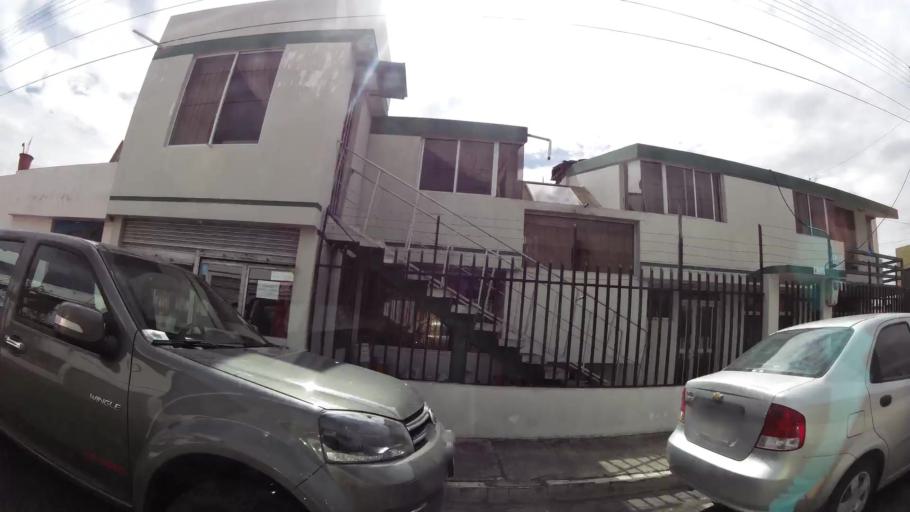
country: EC
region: Cotopaxi
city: Latacunga
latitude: -0.9251
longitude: -78.6231
